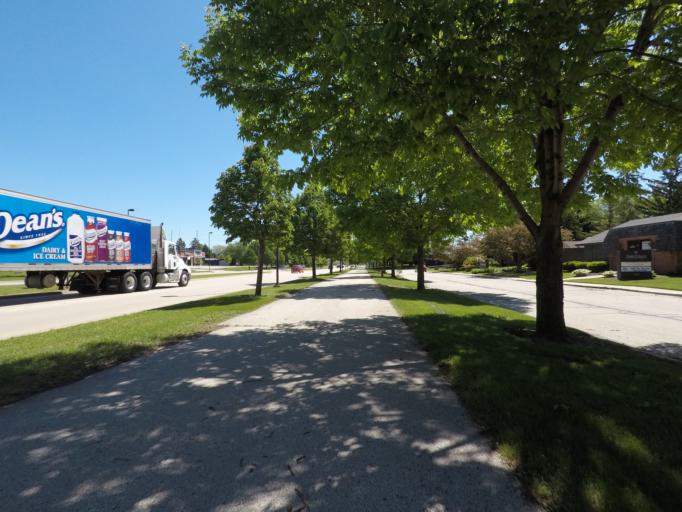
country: US
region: Wisconsin
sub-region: Sheboygan County
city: Sheboygan
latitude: 43.7562
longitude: -87.7358
